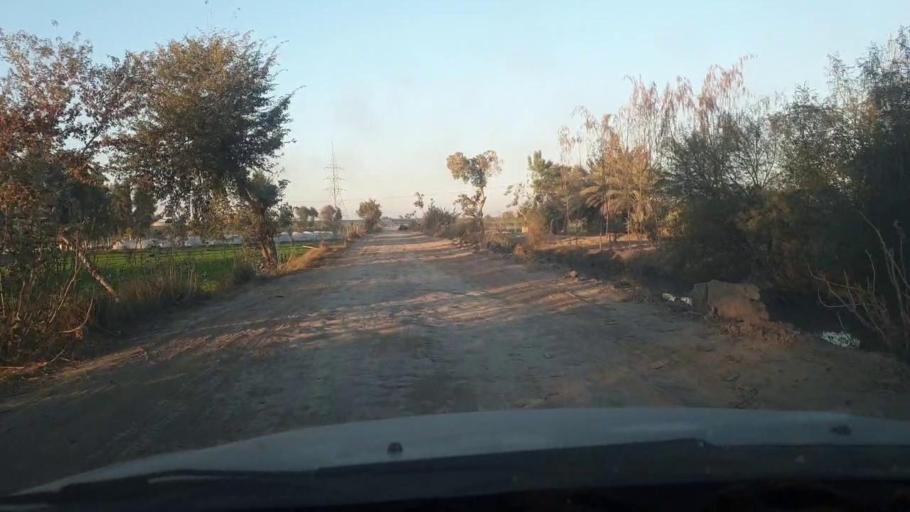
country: PK
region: Sindh
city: Ghotki
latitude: 28.0399
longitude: 69.3244
